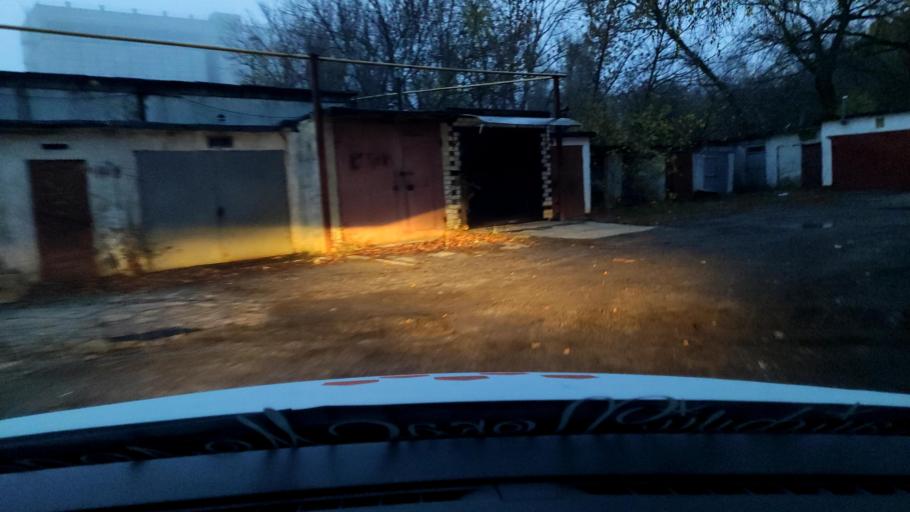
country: RU
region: Voronezj
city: Voronezh
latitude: 51.6789
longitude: 39.1760
